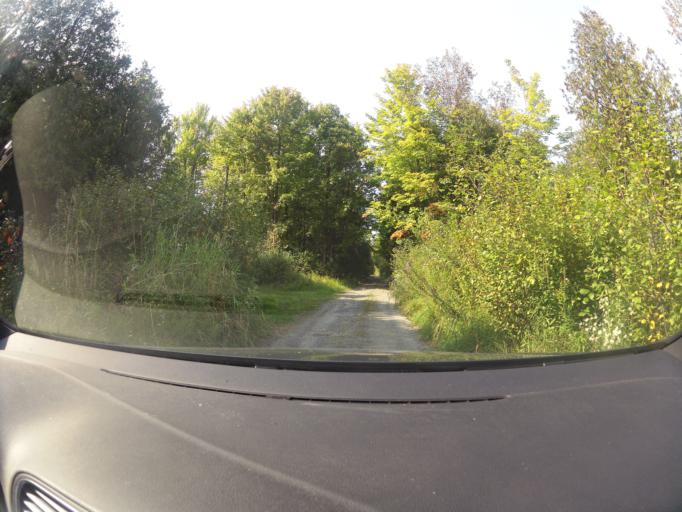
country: CA
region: Ontario
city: Carleton Place
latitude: 45.3134
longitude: -76.1170
